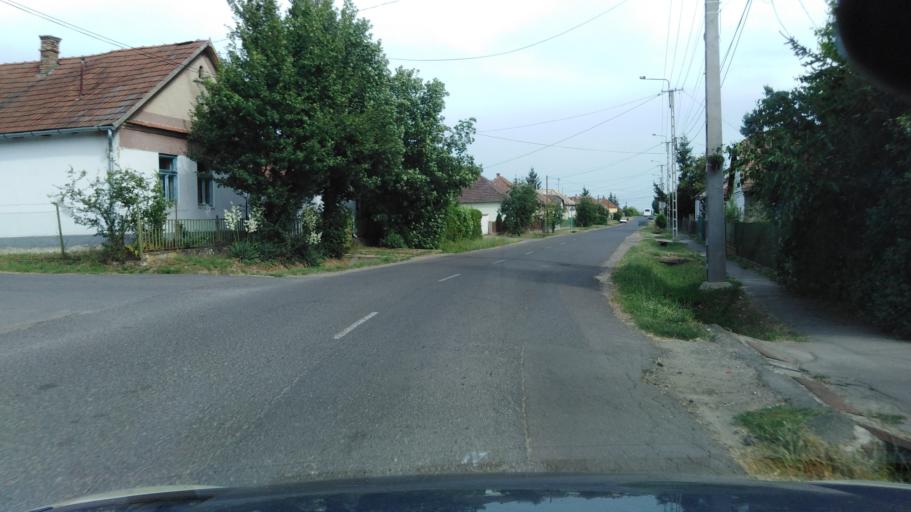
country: HU
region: Nograd
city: Karancskeszi
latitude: 48.2095
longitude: 19.6028
